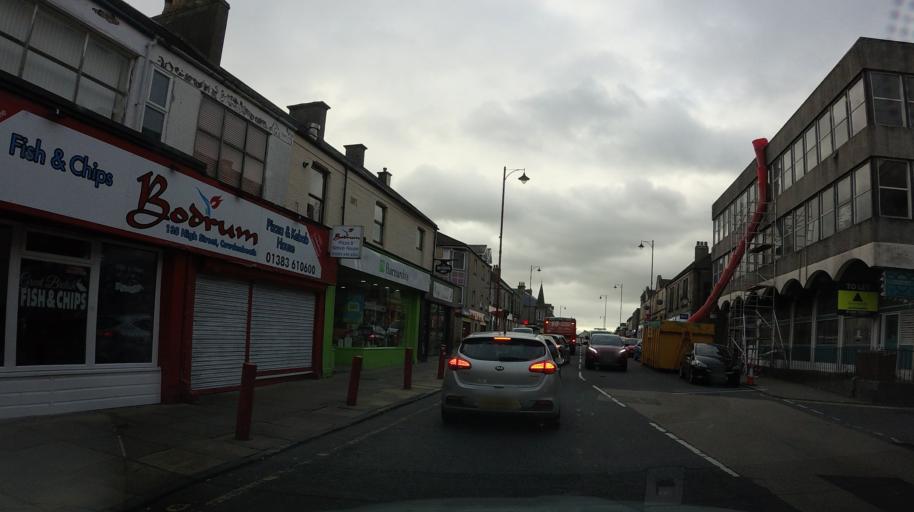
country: GB
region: Scotland
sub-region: Fife
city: Cowdenbeath
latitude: 56.1130
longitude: -3.3446
